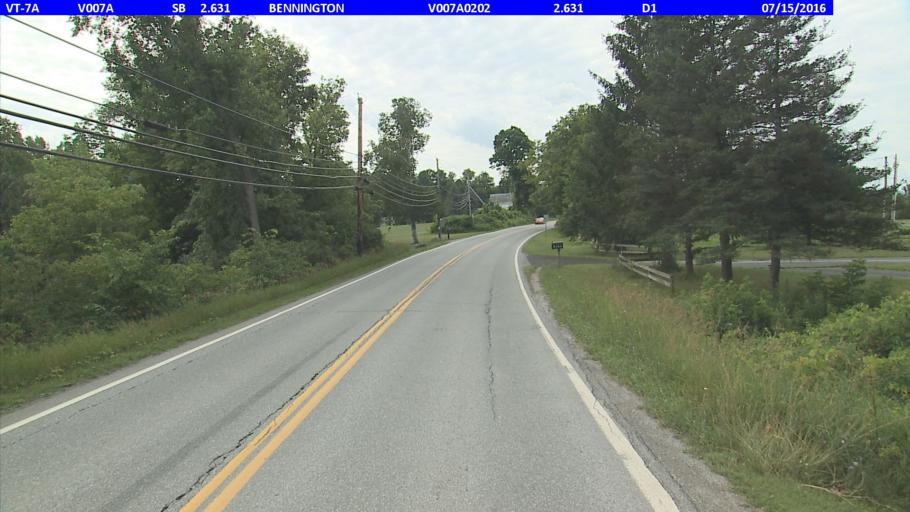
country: US
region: Vermont
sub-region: Bennington County
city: North Bennington
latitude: 42.9273
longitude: -73.2085
